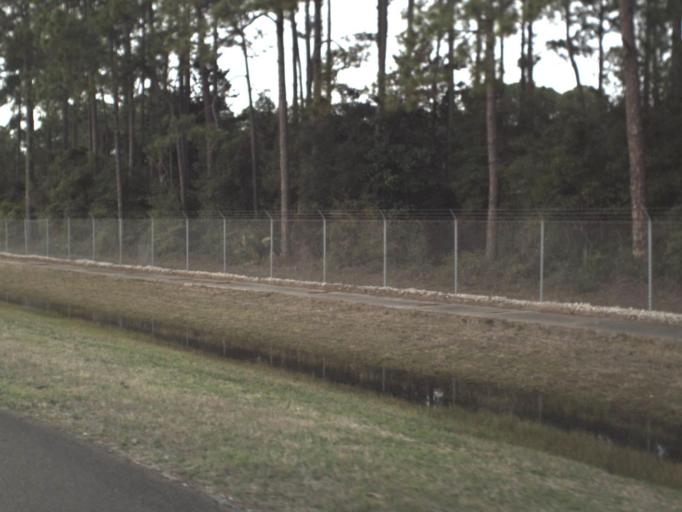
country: US
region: Florida
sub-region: Bay County
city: Tyndall Air Force Base
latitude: 30.0804
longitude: -85.6034
